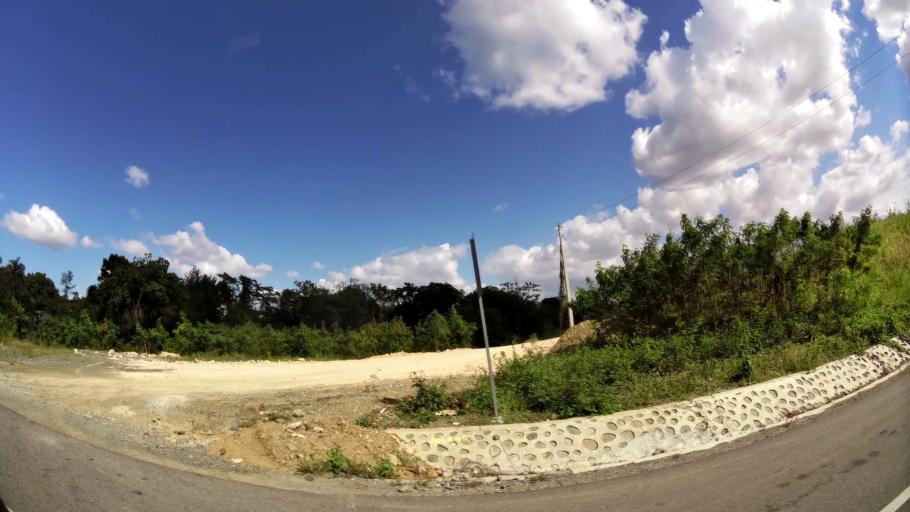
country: DO
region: Santo Domingo
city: Santo Domingo Oeste
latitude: 18.5564
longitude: -70.0712
